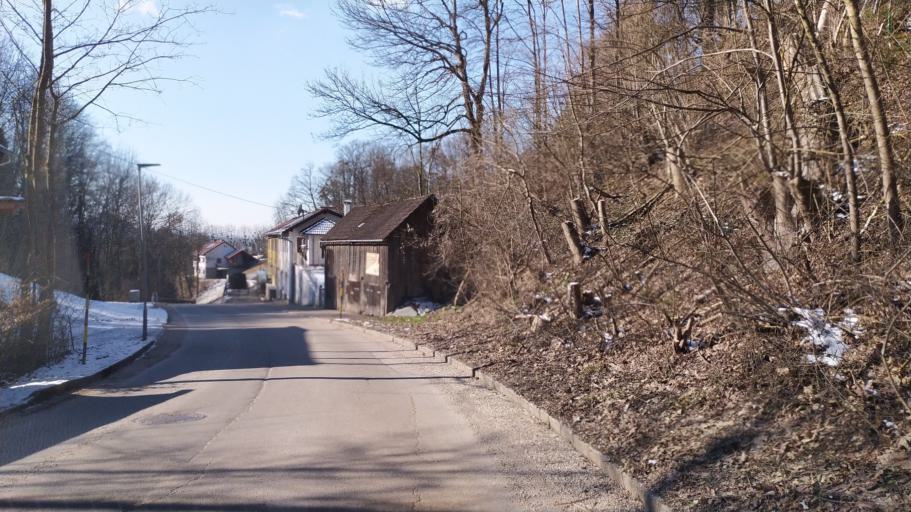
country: AT
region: Upper Austria
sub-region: Politischer Bezirk Urfahr-Umgebung
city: Ottensheim
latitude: 48.3351
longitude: 14.1914
